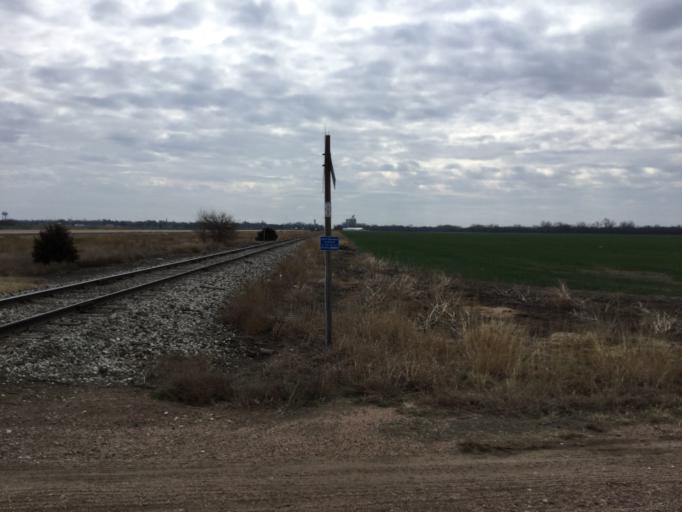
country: US
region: Kansas
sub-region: Barton County
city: Ellinwood
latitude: 38.3594
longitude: -98.6089
